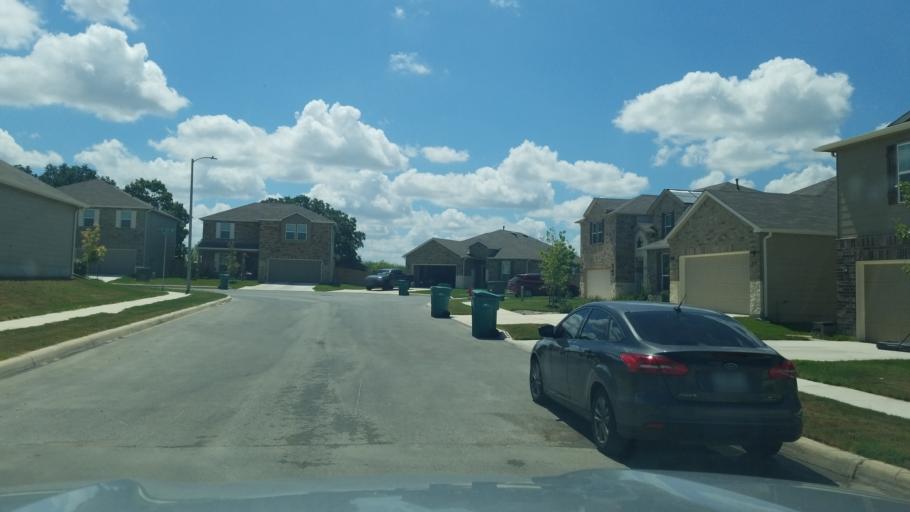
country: US
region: Texas
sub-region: Bexar County
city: Converse
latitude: 29.5344
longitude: -98.3162
